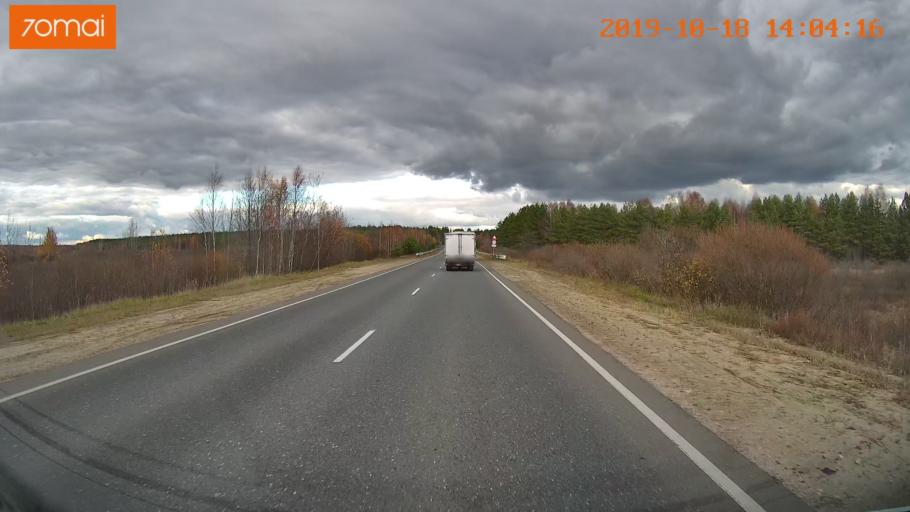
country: RU
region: Rjazan
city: Spas-Klepiki
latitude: 55.1241
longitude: 40.1335
